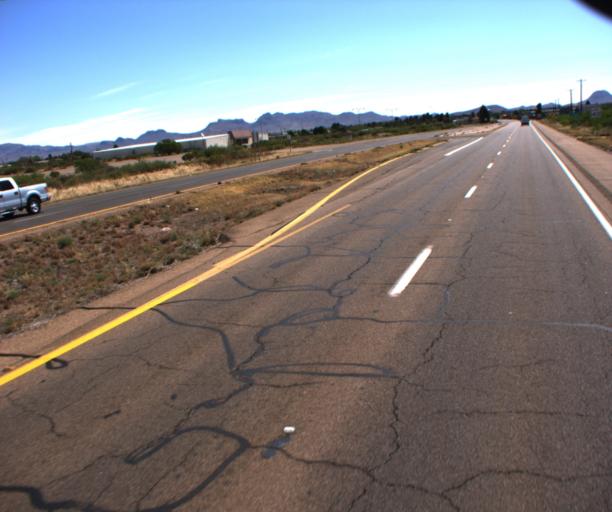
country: US
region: Arizona
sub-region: Cochise County
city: Pirtleville
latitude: 31.3511
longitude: -109.5679
